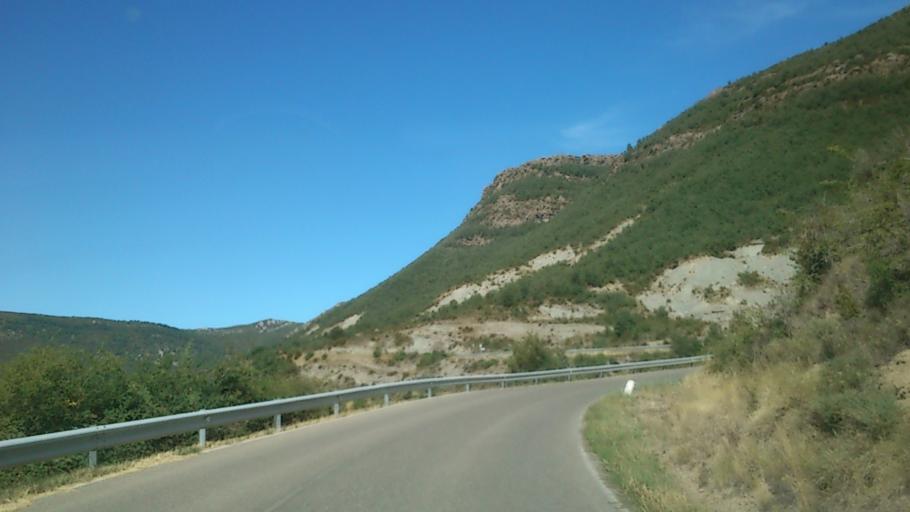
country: ES
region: Aragon
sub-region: Provincia de Huesca
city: Arguis
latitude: 42.3160
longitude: -0.4403
